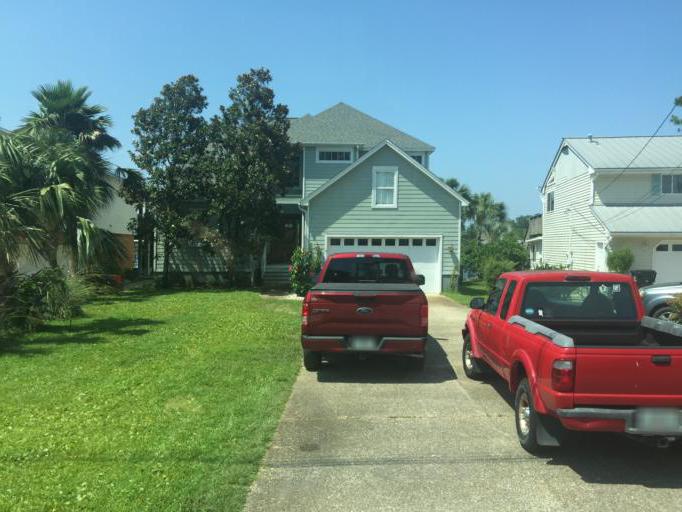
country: US
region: Florida
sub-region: Bay County
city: Lower Grand Lagoon
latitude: 30.1608
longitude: -85.7730
